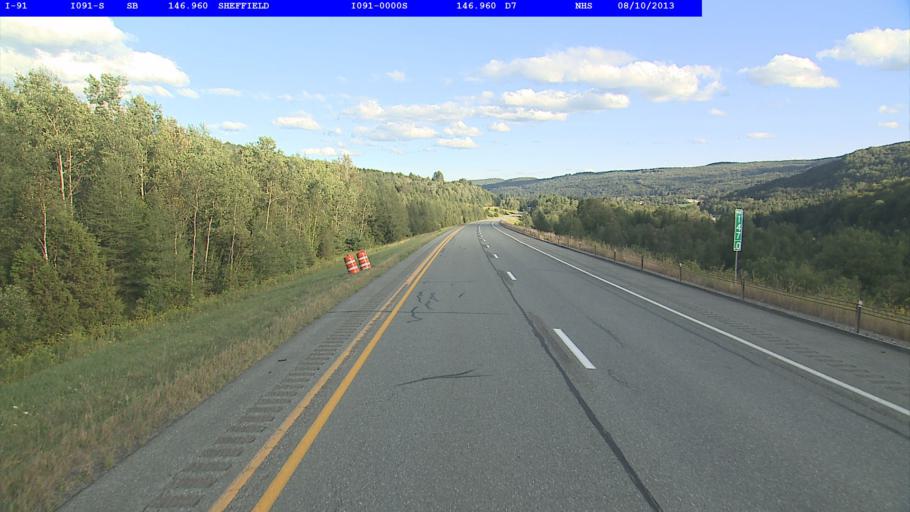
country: US
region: Vermont
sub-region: Caledonia County
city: Lyndonville
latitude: 44.6218
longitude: -72.1243
